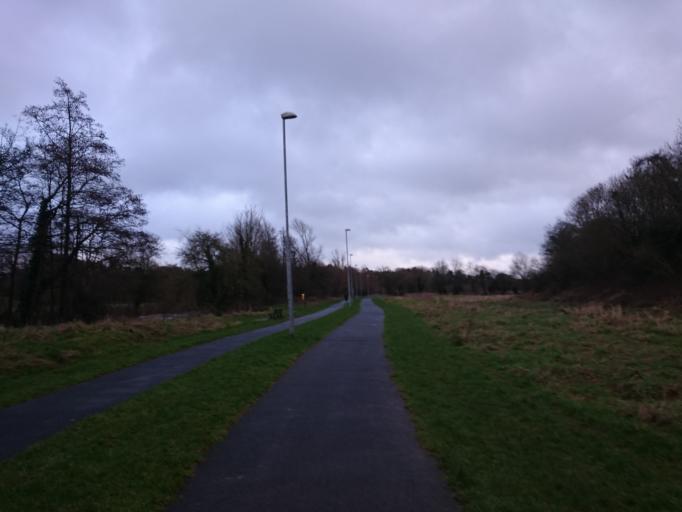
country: IE
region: Leinster
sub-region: Kilkenny
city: Kilkenny
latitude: 52.6671
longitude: -7.2585
